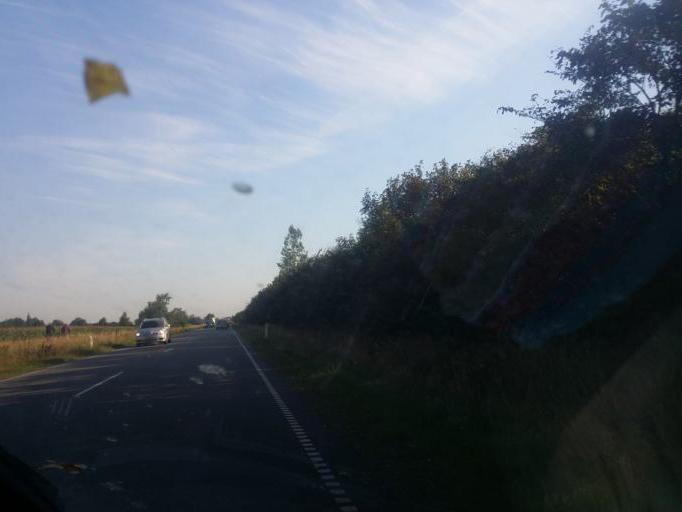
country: DK
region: South Denmark
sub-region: Esbjerg Kommune
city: Ribe
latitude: 55.3082
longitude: 8.7472
